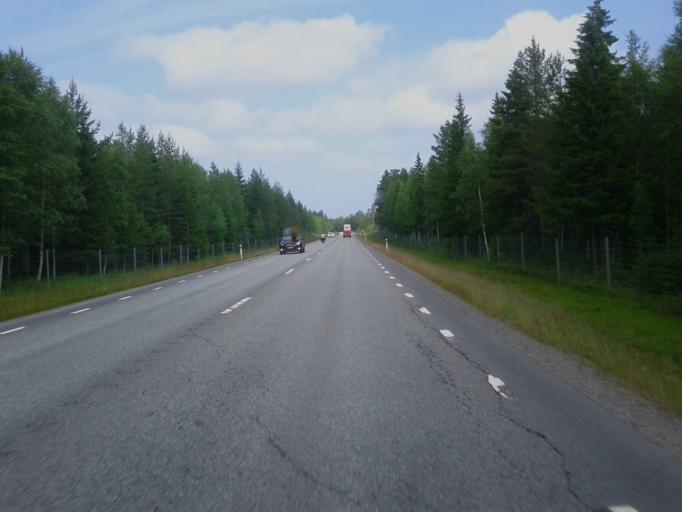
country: SE
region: Vaesterbotten
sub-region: Skelleftea Kommun
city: Burea
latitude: 64.4728
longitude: 21.2917
